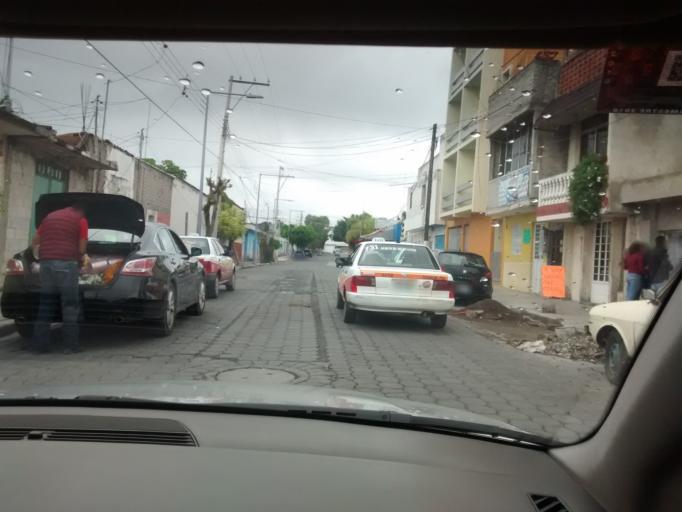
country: MX
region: Puebla
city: Tehuacan
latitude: 18.4582
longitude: -97.3989
